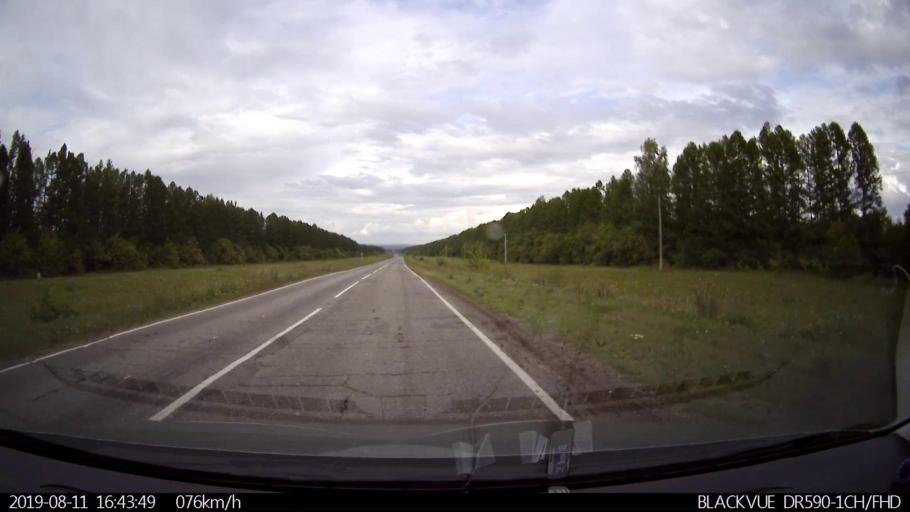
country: RU
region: Ulyanovsk
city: Mayna
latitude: 54.1722
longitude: 47.6756
